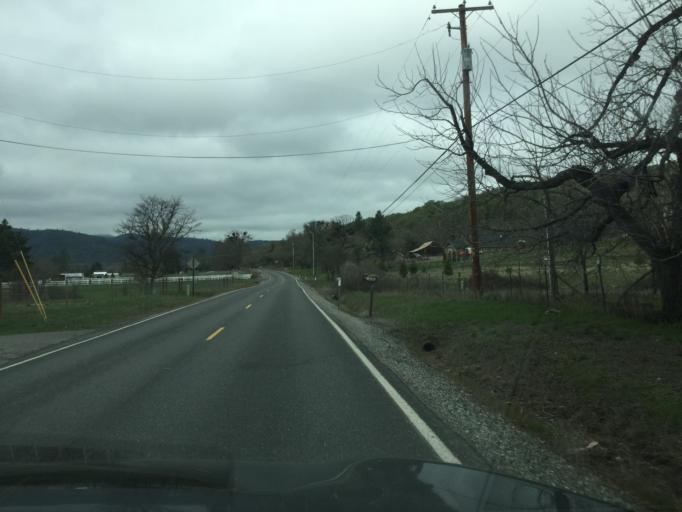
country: US
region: Oregon
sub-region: Jackson County
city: Gold Hill
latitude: 42.3940
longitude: -122.9974
